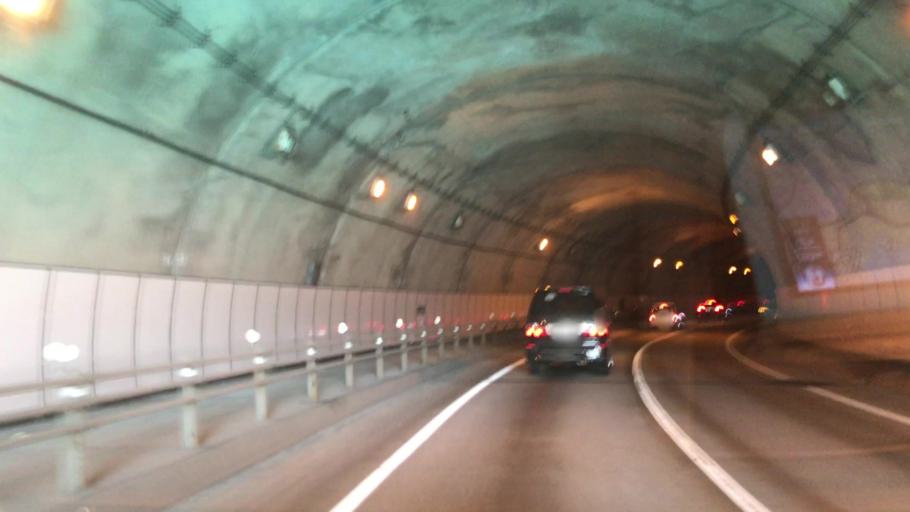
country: JP
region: Hokkaido
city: Otaru
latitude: 43.1613
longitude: 141.0342
